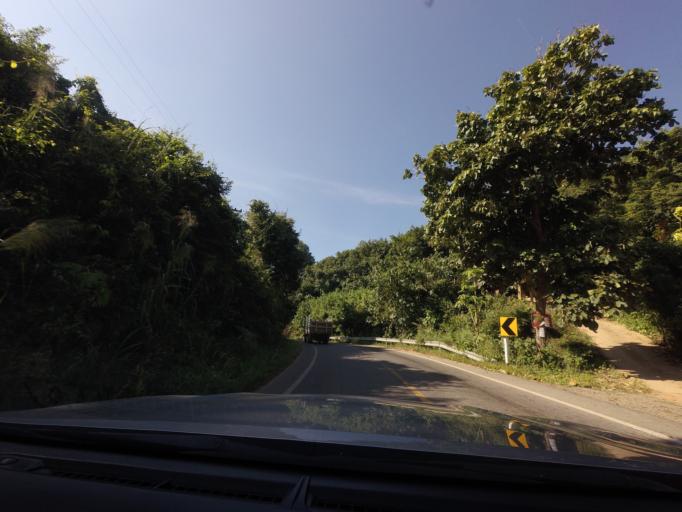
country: TH
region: Phrae
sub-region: Amphoe Wang Chin
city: Wang Chin
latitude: 17.7079
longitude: 99.6916
